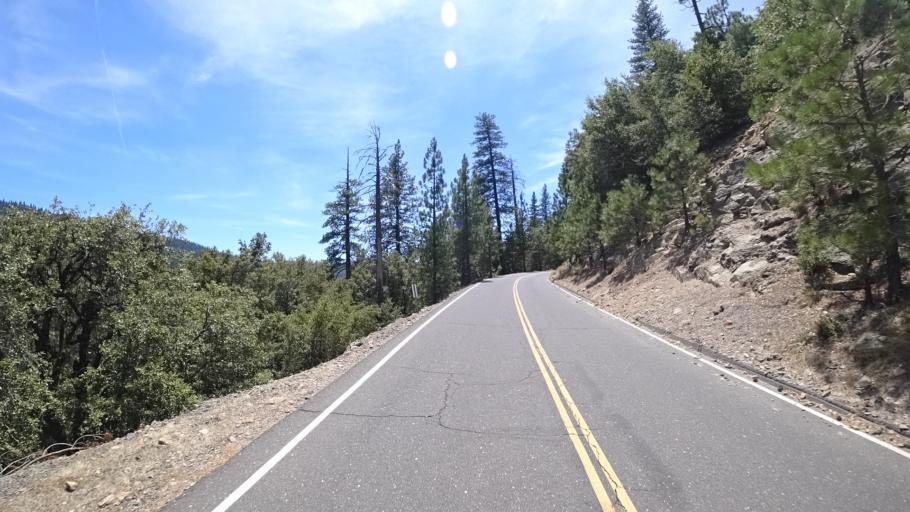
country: US
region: California
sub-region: Calaveras County
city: Arnold
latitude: 38.3151
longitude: -120.2311
